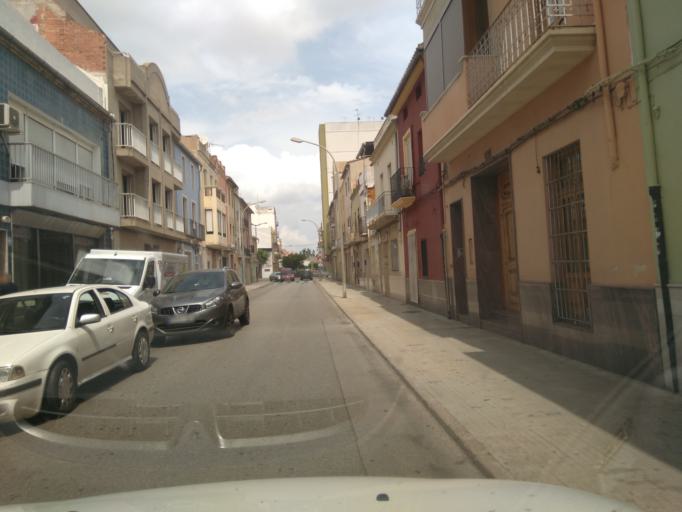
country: ES
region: Valencia
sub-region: Provincia de Valencia
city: Carcaixent
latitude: 39.1255
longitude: -0.4499
